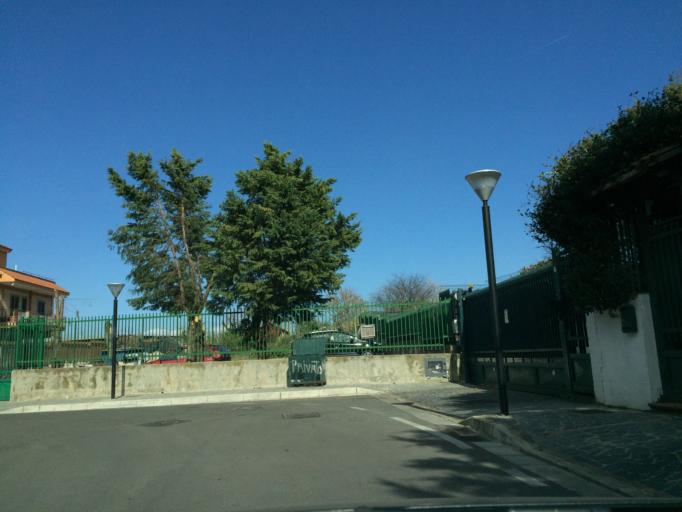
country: IT
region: Campania
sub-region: Provincia di Napoli
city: Pollena Trocchia
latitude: 40.8500
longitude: 14.3829
